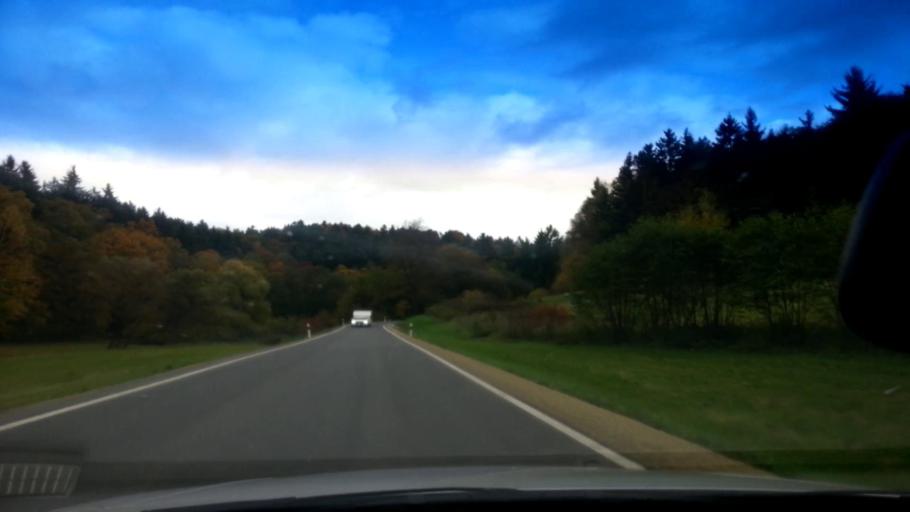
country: DE
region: Bavaria
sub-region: Upper Franconia
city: Wonsees
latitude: 49.9877
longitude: 11.2948
